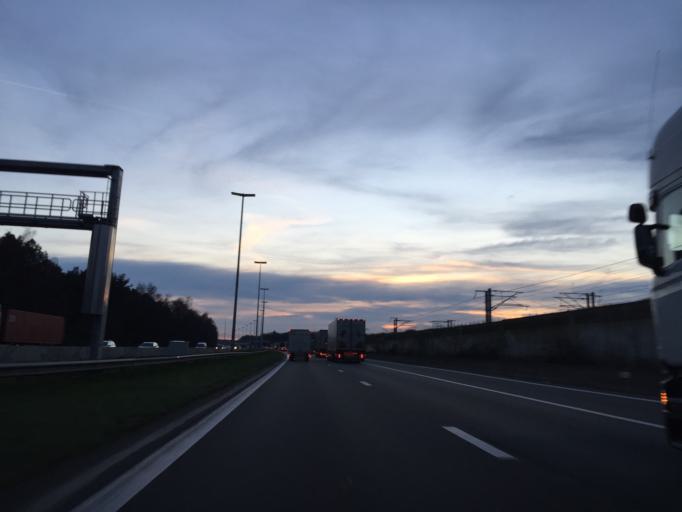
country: BE
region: Flanders
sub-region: Provincie Antwerpen
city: Brasschaat
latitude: 51.2888
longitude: 4.5173
